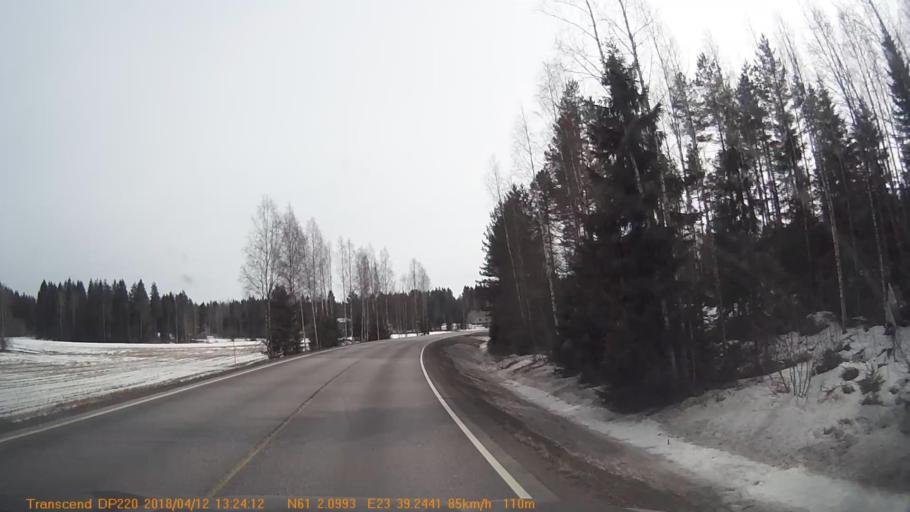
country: FI
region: Pirkanmaa
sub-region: Etelae-Pirkanmaa
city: Kylmaekoski
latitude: 61.0340
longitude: 23.6552
